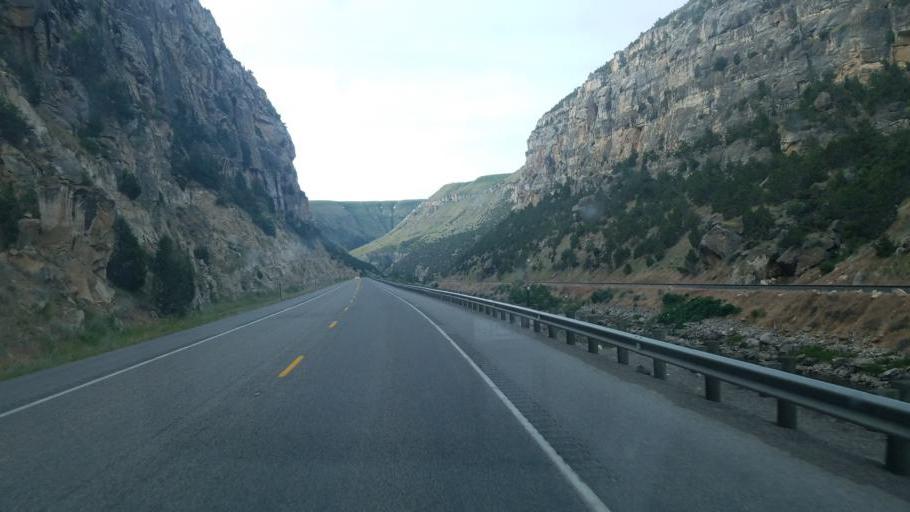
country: US
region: Wyoming
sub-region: Hot Springs County
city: Thermopolis
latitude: 43.5712
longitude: -108.2112
